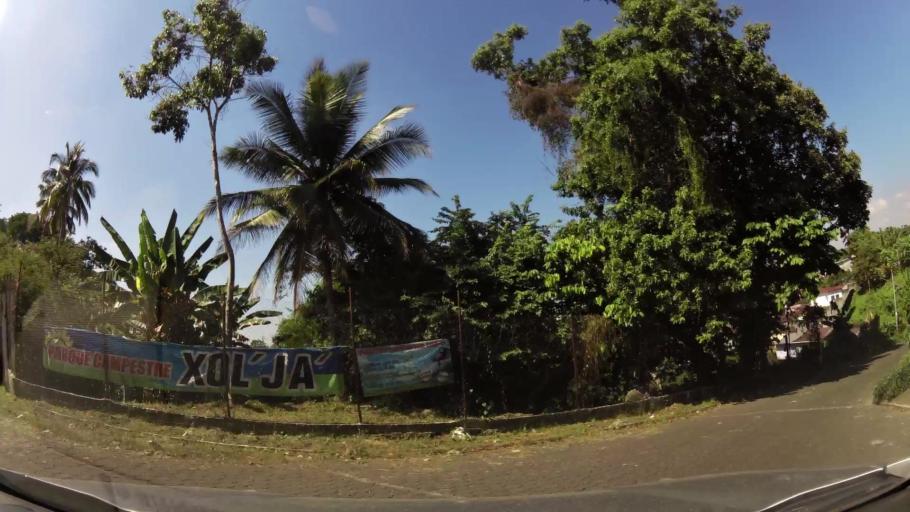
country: GT
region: Suchitepeque
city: Mazatenango
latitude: 14.5331
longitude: -91.4996
